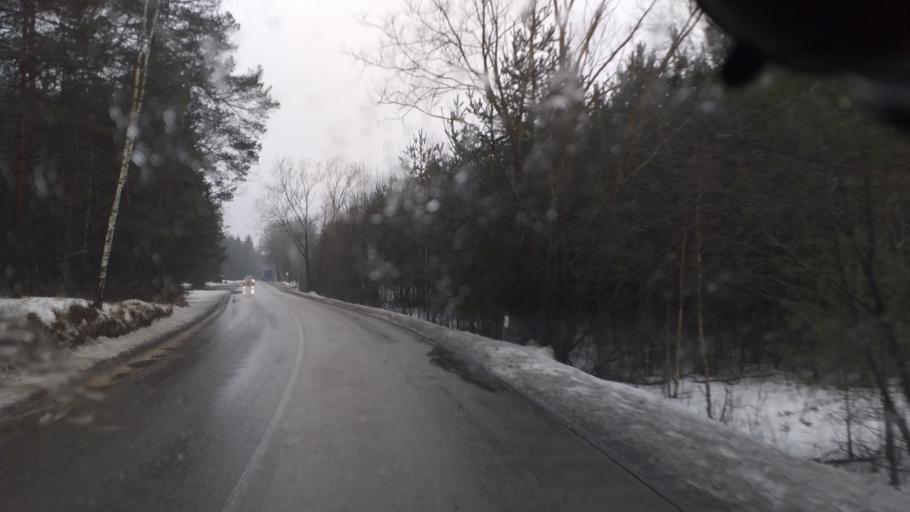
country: LV
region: Babite
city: Pinki
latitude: 56.9794
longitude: 23.9780
